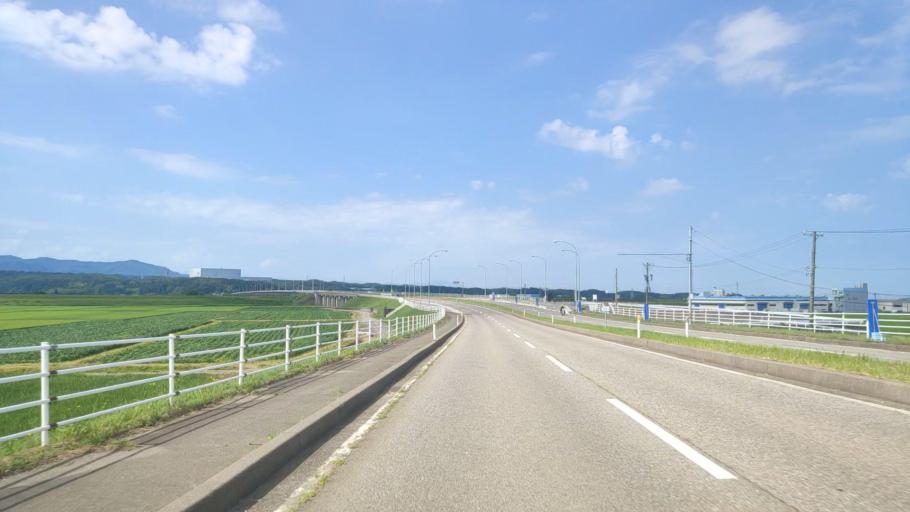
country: JP
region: Ishikawa
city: Matsuto
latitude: 36.4662
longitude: 136.5784
